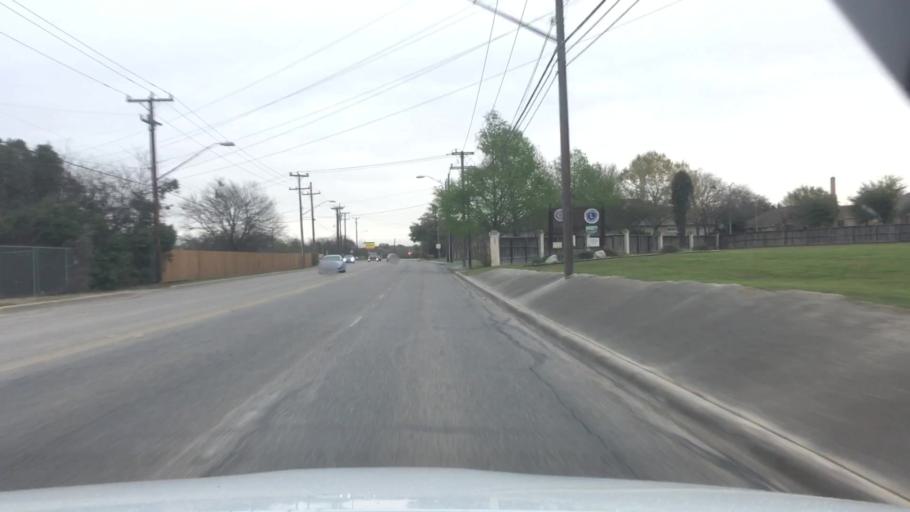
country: US
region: Texas
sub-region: Bexar County
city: Windcrest
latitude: 29.5230
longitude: -98.3843
